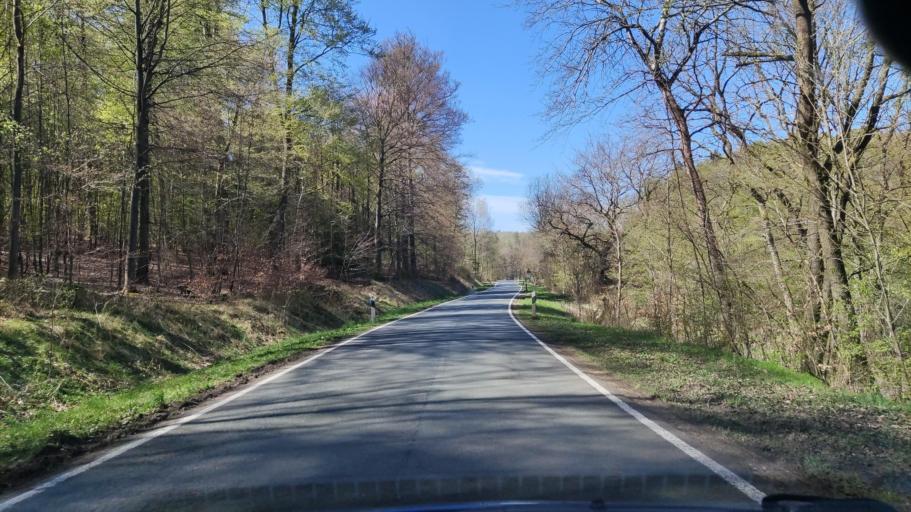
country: DE
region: Lower Saxony
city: Eimen
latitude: 51.9070
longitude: 9.7785
